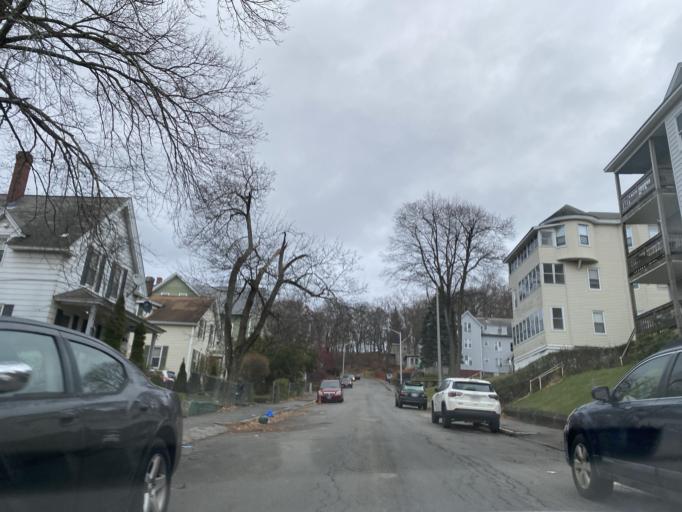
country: US
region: Massachusetts
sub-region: Worcester County
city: Worcester
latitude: 42.2808
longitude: -71.7916
